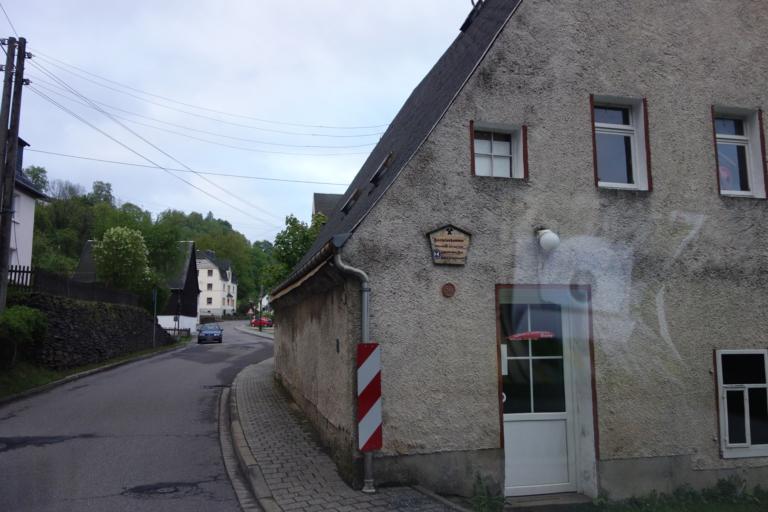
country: DE
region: Saxony
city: Pobershau
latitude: 50.6404
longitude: 13.2187
